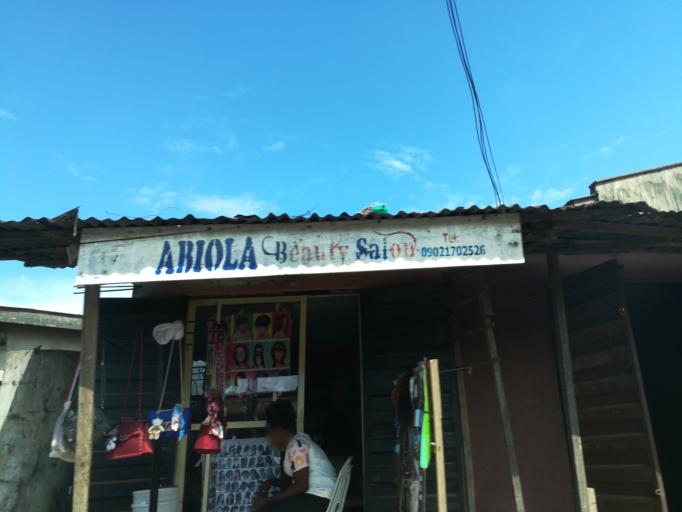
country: NG
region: Lagos
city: Ikorodu
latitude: 6.5950
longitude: 3.5182
